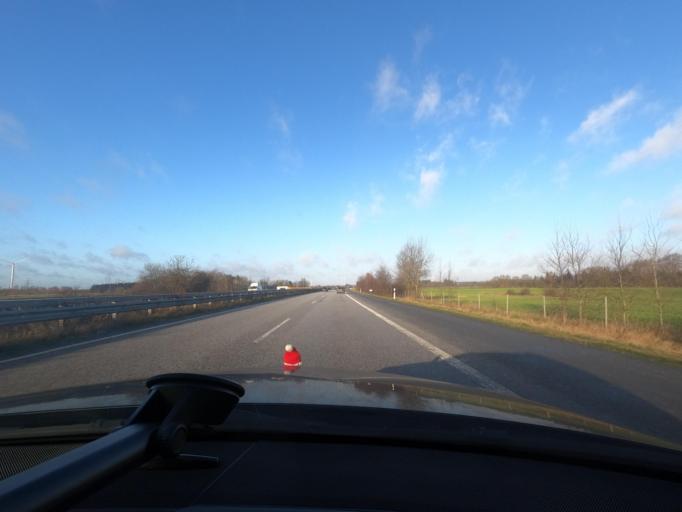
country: DE
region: Schleswig-Holstein
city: Bollingstedt
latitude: 54.6139
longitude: 9.4446
